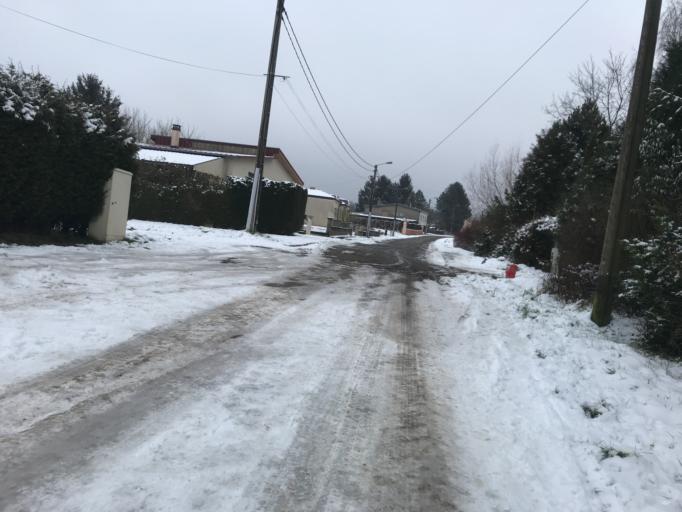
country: FR
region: Lorraine
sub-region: Departement de la Moselle
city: Russange
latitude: 49.4897
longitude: 5.9471
